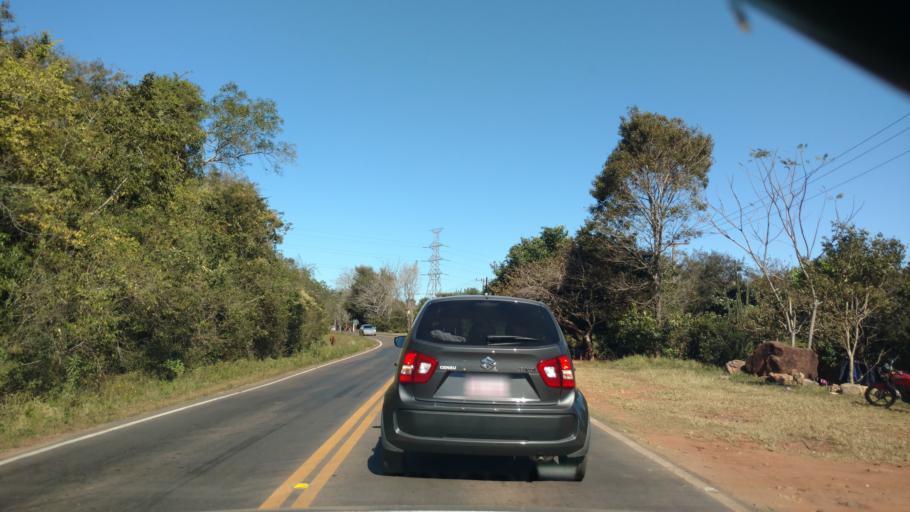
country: PY
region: Paraguari
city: Pirayu
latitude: -25.4945
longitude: -57.2449
